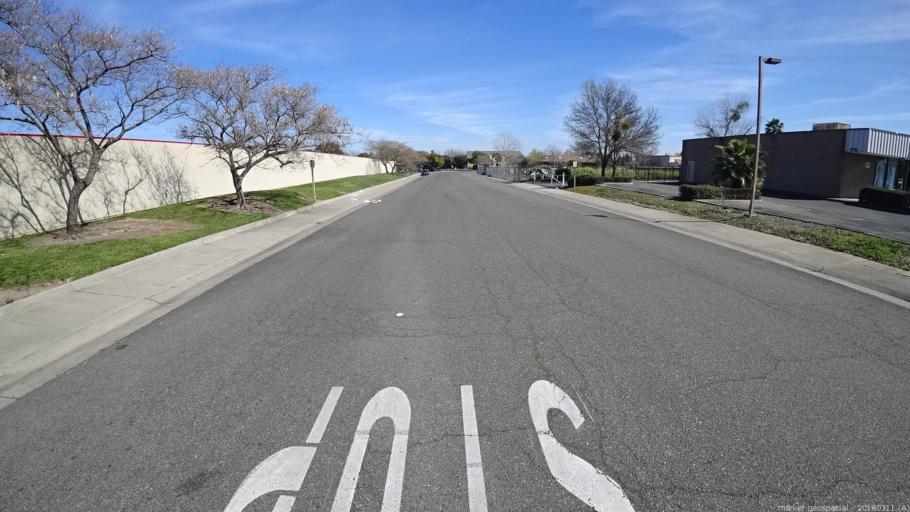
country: US
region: California
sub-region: Sacramento County
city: Parkway
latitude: 38.4935
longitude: -121.4411
